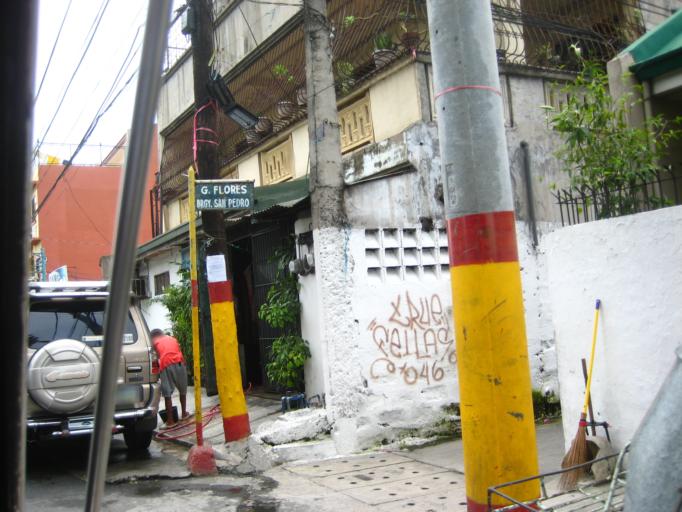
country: PH
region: Calabarzon
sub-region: Province of Rizal
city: Pateros
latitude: 14.5460
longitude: 121.0672
